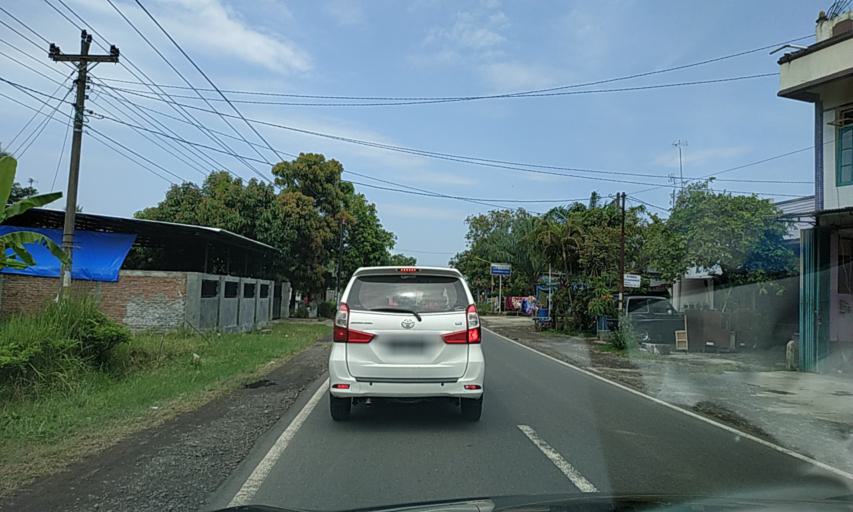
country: ID
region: Central Java
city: Mulyosari
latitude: -7.4961
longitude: 108.7896
